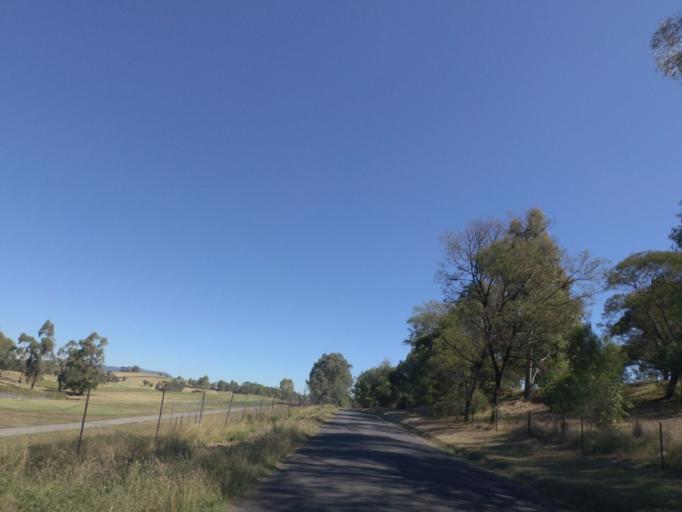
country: AU
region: Victoria
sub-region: Yarra Ranges
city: Chirnside Park
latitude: -37.7166
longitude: 145.2929
